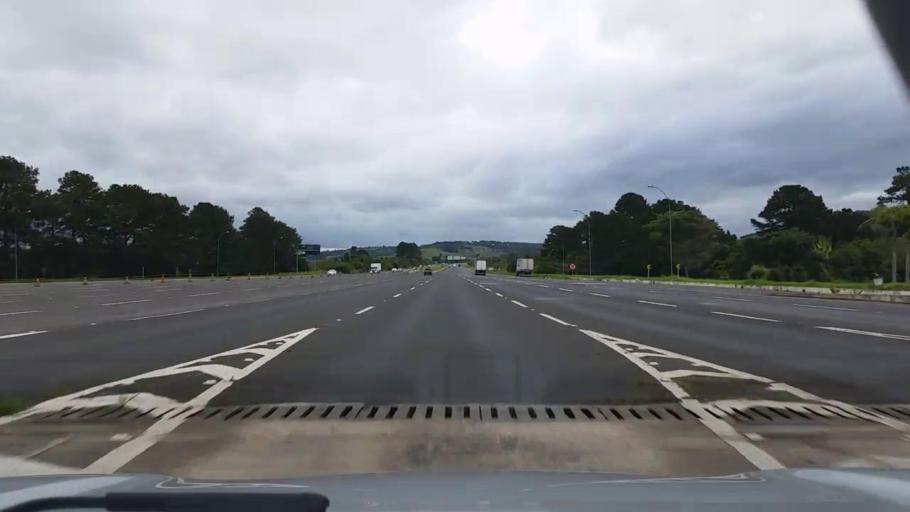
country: BR
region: Rio Grande do Sul
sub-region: Osorio
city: Osorio
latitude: -29.8856
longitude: -50.4489
